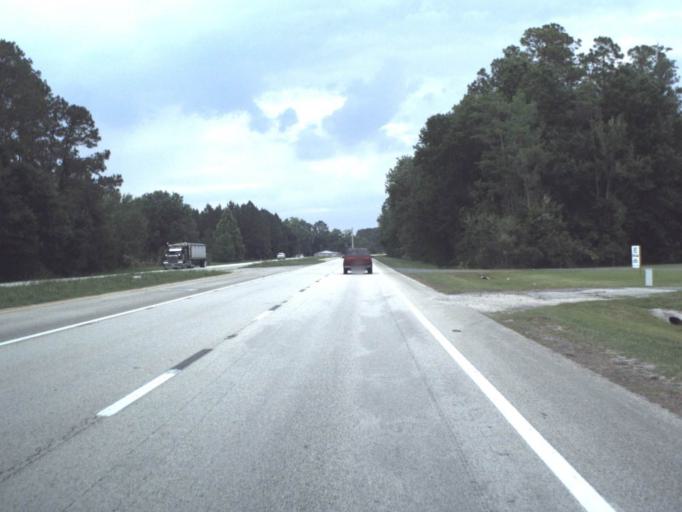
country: US
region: Florida
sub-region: Bradford County
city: Starke
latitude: 30.0683
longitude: -82.0660
